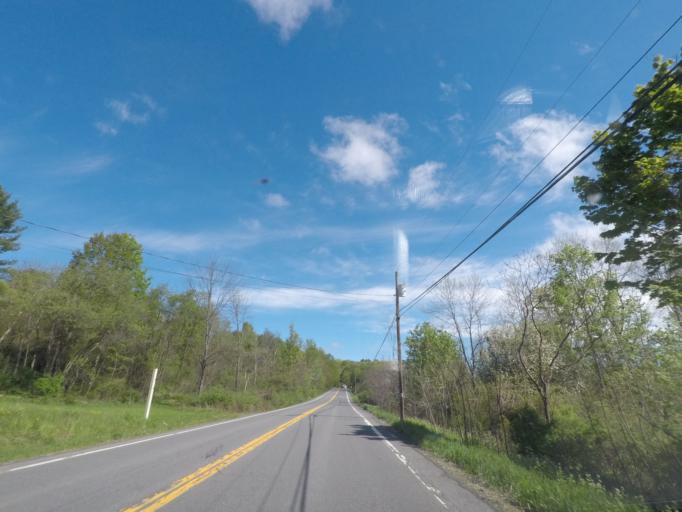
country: US
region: New York
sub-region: Albany County
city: Ravena
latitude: 42.4778
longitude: -73.9250
